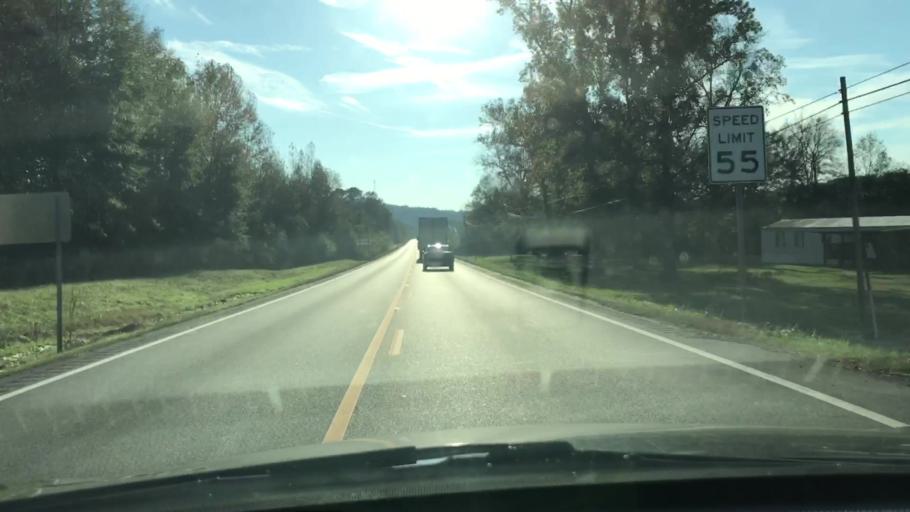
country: US
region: Alabama
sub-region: Calhoun County
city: Choccolocco
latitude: 33.6455
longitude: -85.6588
